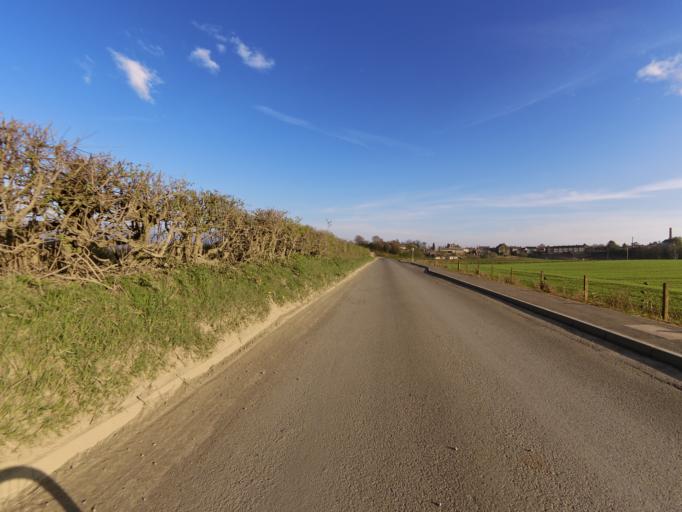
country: GB
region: Scotland
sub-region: Fife
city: Leslie
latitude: 56.2084
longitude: -3.2061
